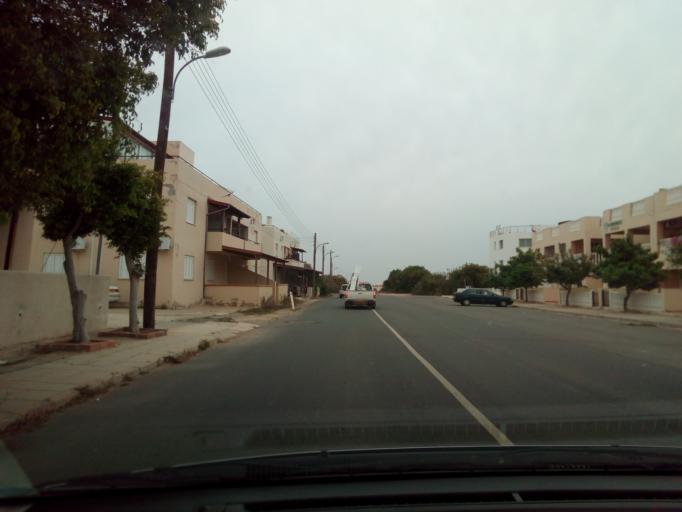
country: CY
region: Ammochostos
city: Paralimni
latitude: 35.0558
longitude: 34.0005
